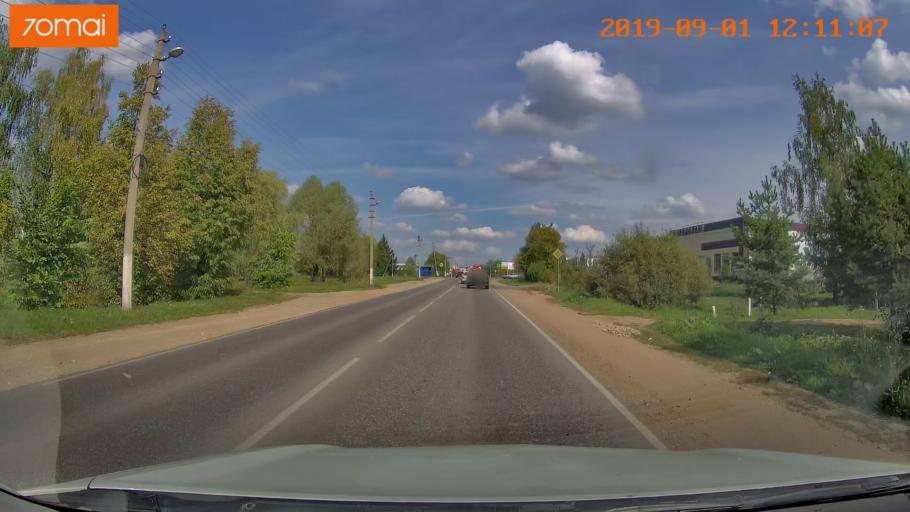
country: RU
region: Kaluga
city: Maloyaroslavets
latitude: 54.9973
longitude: 36.4376
